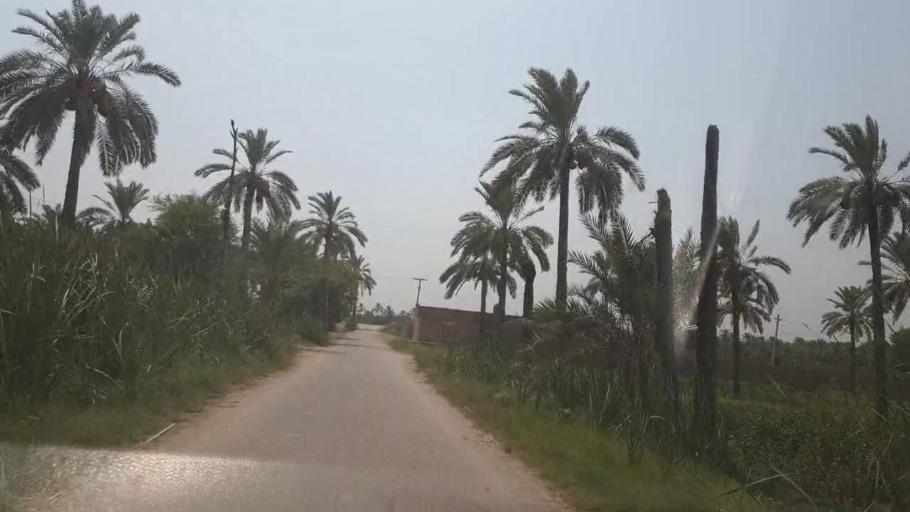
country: PK
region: Sindh
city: Khairpur
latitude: 27.4693
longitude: 68.7558
